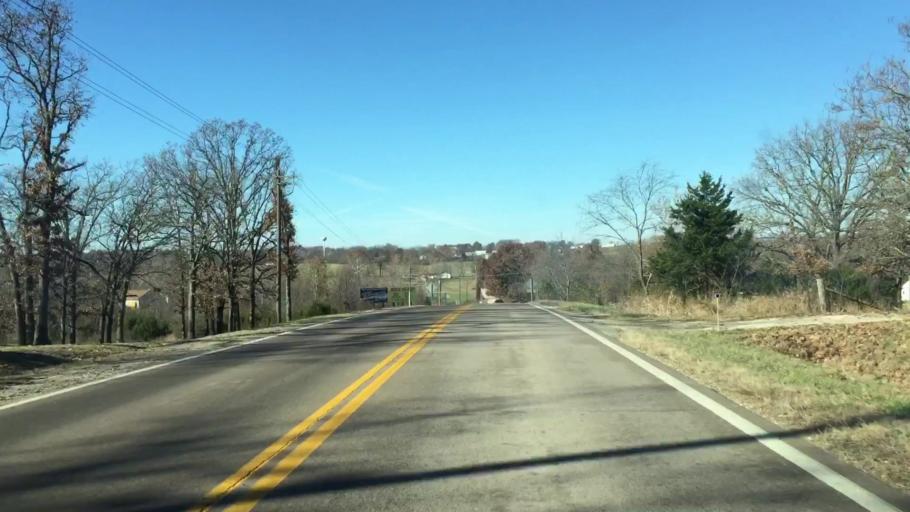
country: US
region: Missouri
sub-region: Miller County
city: Eldon
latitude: 38.3642
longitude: -92.5530
